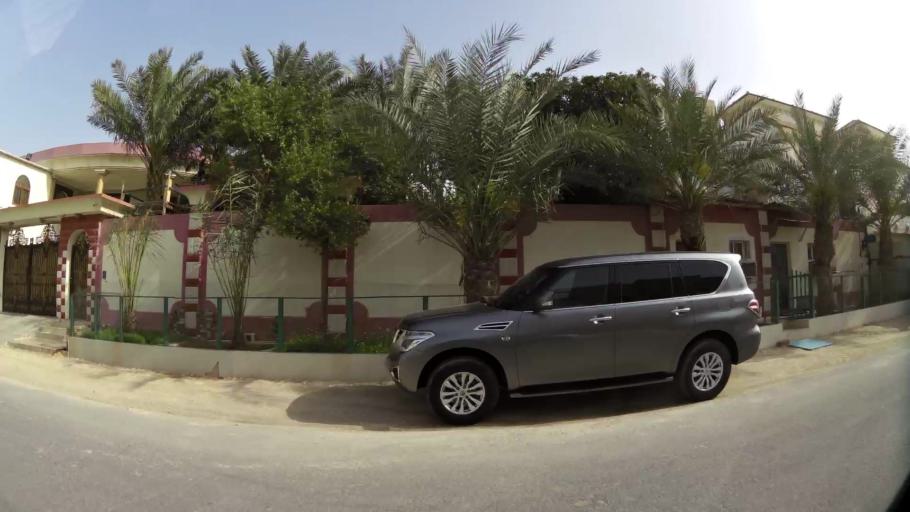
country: QA
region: Baladiyat ar Rayyan
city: Ar Rayyan
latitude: 25.2423
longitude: 51.4465
